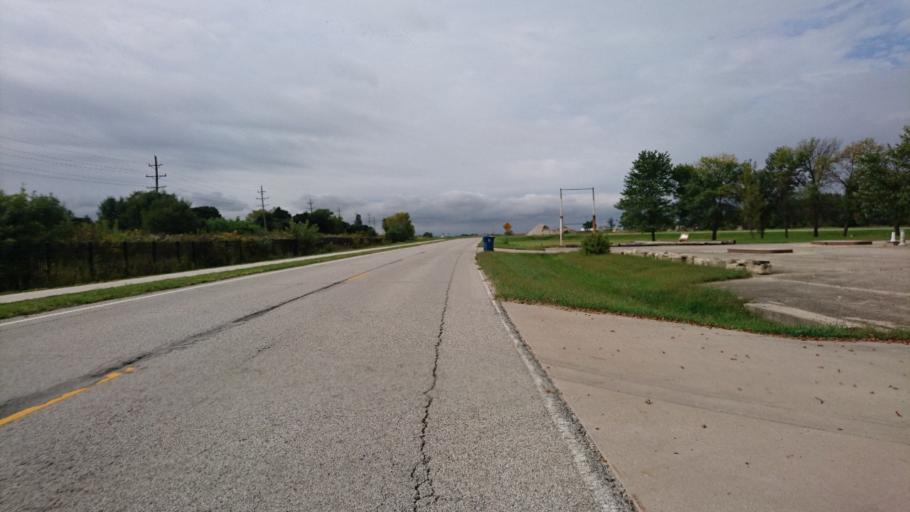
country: US
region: Illinois
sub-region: Livingston County
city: Dwight
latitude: 41.0821
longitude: -88.4415
